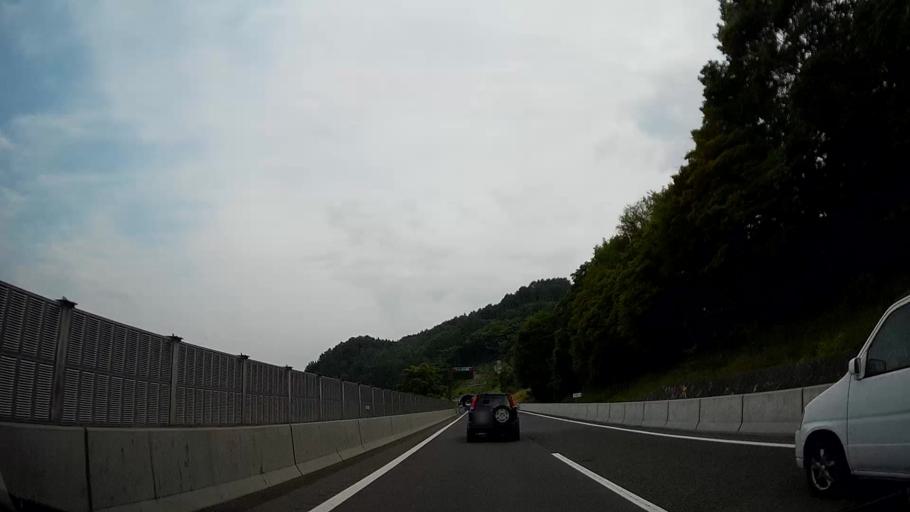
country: JP
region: Nagano
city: Okaya
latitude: 36.0474
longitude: 138.0530
